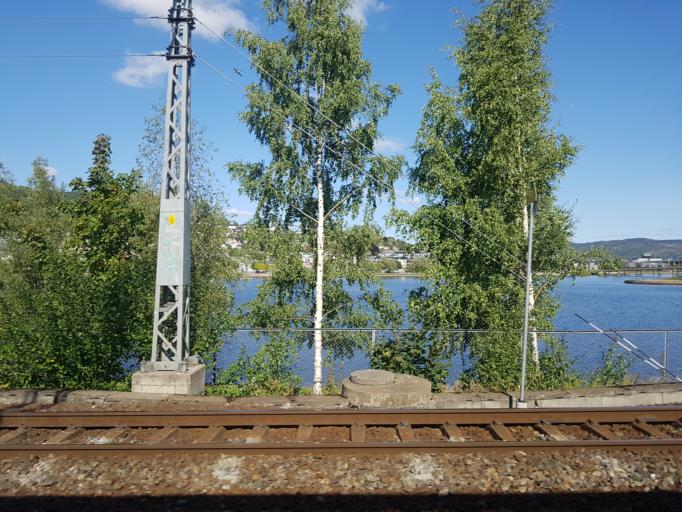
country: NO
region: Buskerud
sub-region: Drammen
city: Drammen
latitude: 59.7375
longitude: 10.2116
